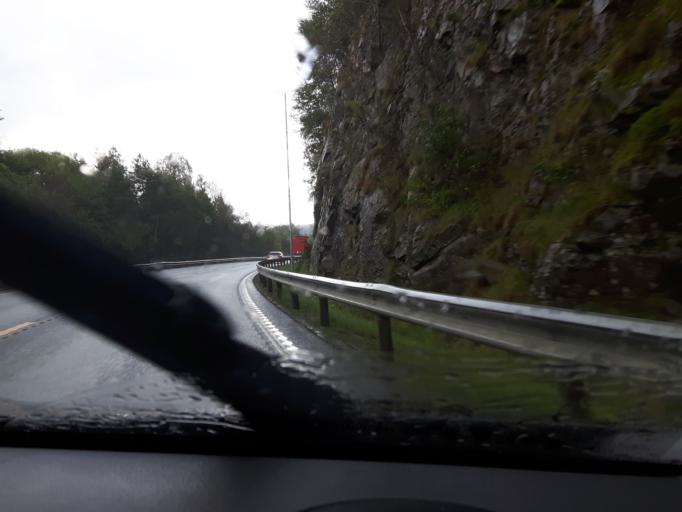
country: NO
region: Vest-Agder
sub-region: Sogne
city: Sogne
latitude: 58.0965
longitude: 7.7162
